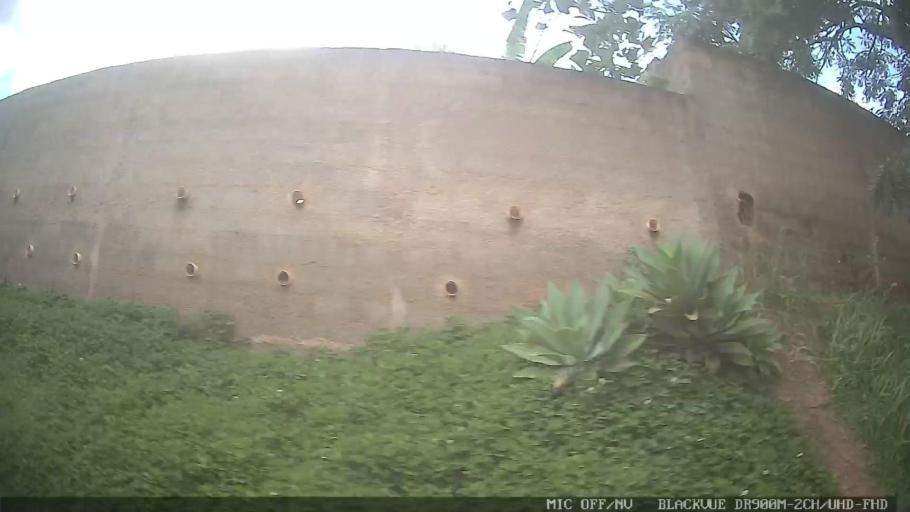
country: BR
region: Sao Paulo
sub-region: Braganca Paulista
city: Braganca Paulista
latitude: -23.0314
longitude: -46.5291
